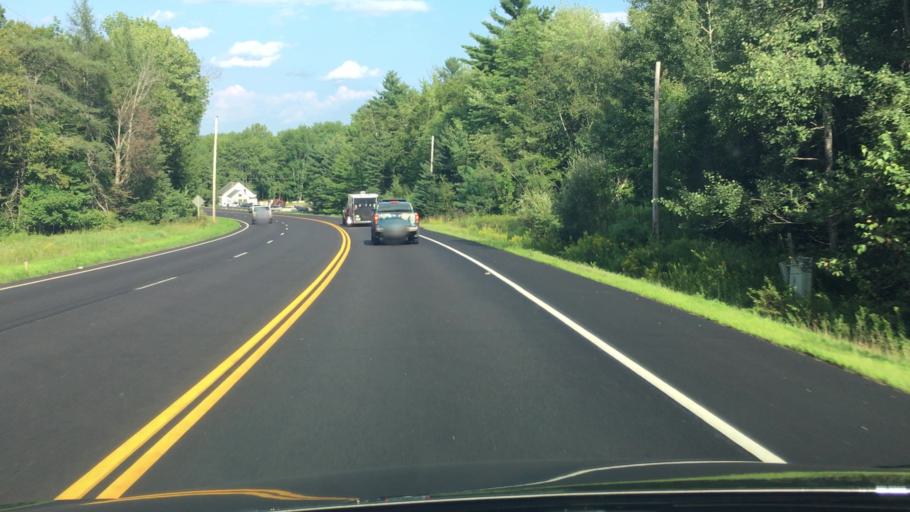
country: US
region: Maine
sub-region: Waldo County
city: Searsmont
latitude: 44.3999
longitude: -69.2475
